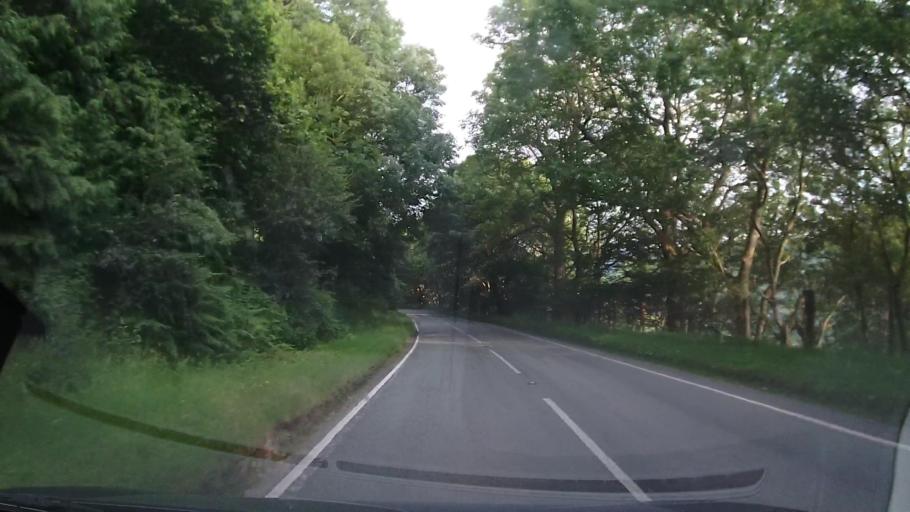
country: GB
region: Wales
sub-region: Sir Powys
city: Llangynog
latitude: 52.8478
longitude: -3.4299
